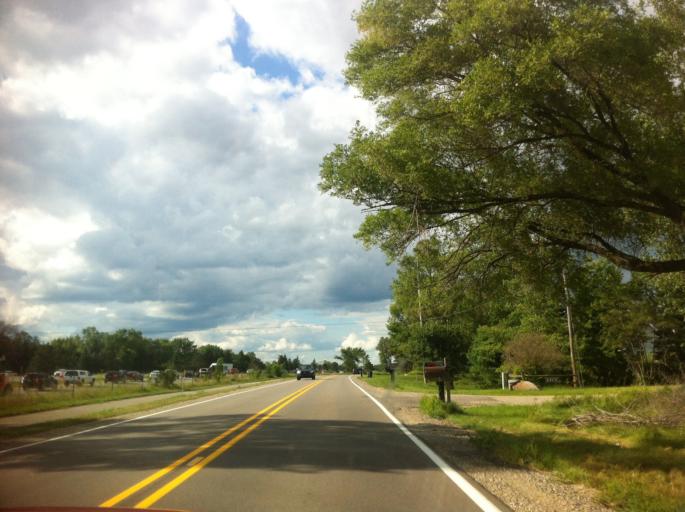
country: US
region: Michigan
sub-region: Livingston County
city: Whitmore Lake
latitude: 42.4833
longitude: -83.7562
